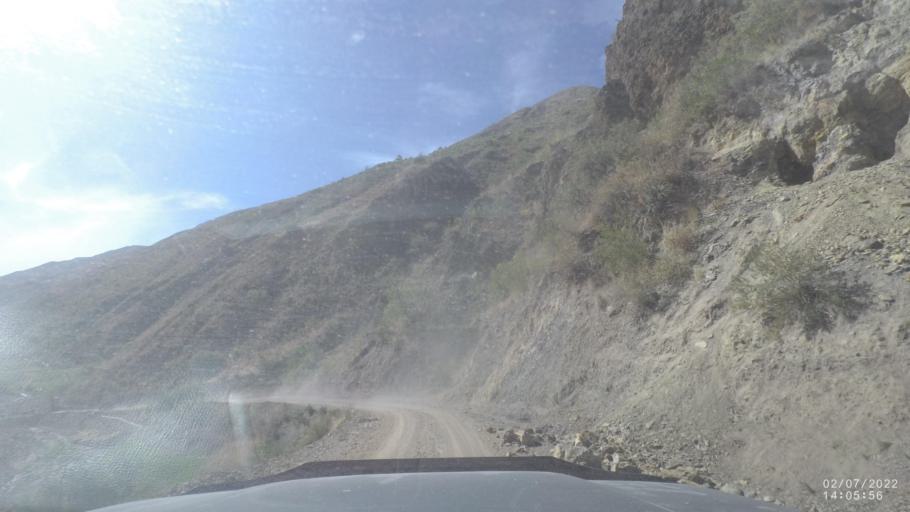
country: BO
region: Cochabamba
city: Irpa Irpa
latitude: -17.8196
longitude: -66.3982
